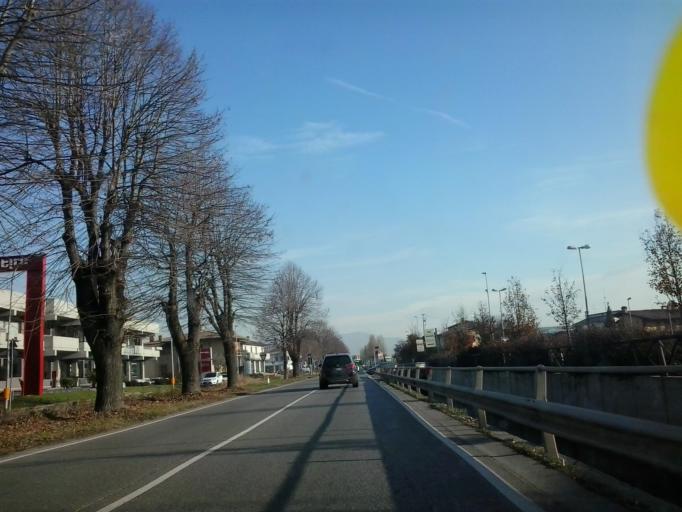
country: IT
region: Lombardy
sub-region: Provincia di Brescia
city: Capriano del Colle
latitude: 45.4756
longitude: 10.1327
